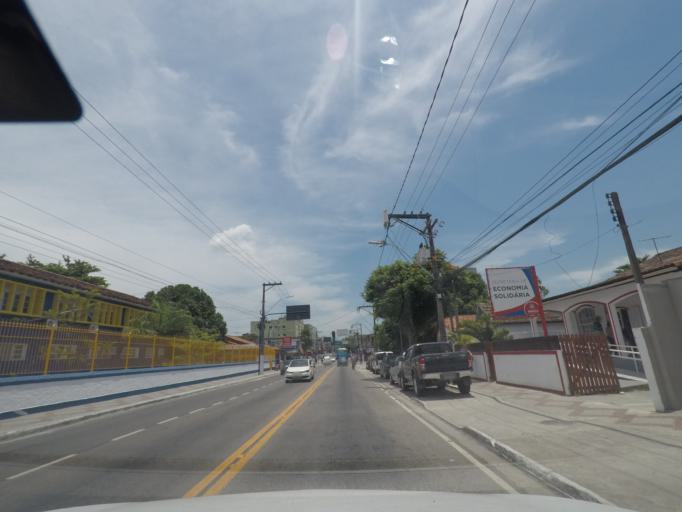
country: BR
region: Rio de Janeiro
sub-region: Marica
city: Marica
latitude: -22.9180
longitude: -42.8185
